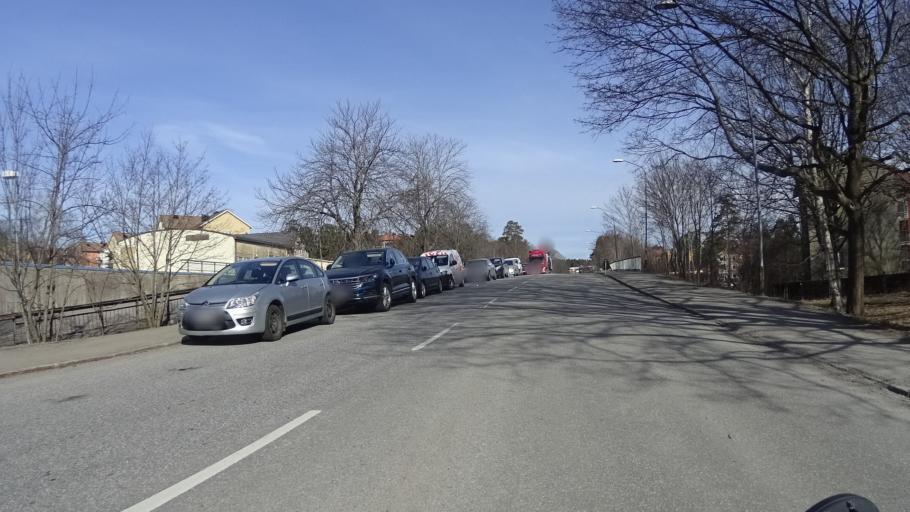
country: SE
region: Stockholm
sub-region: Nacka Kommun
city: Nacka
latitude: 59.2770
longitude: 18.1274
